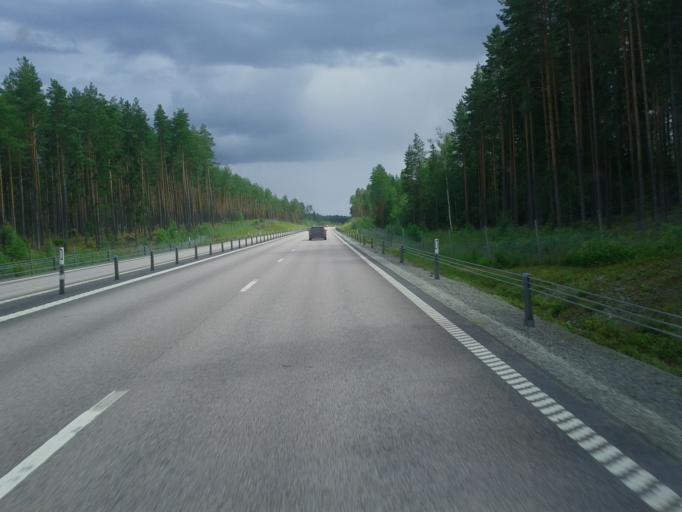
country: SE
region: Vaestmanland
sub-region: Sala Kommun
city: Sala
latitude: 59.9373
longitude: 16.5148
